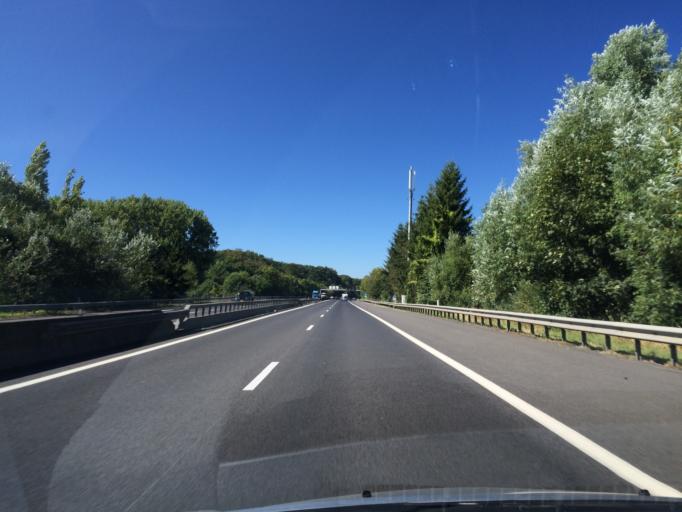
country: LU
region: Luxembourg
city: Capellen
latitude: 49.6373
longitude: 5.9992
